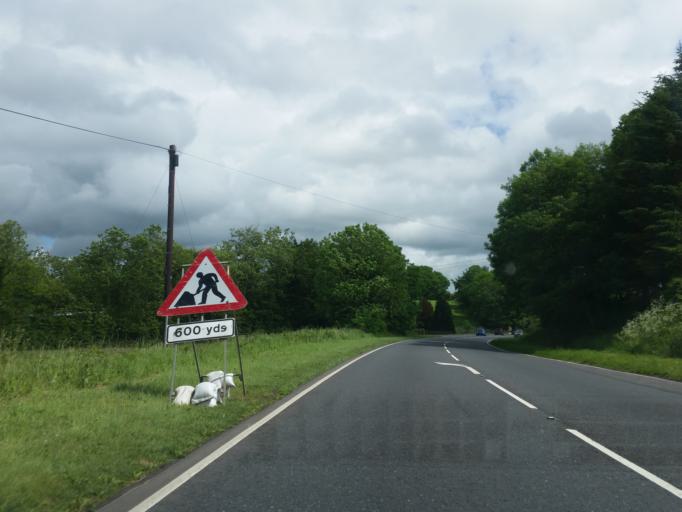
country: IE
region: Ulster
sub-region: County Monaghan
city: Monaghan
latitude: 54.4730
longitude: -7.0560
